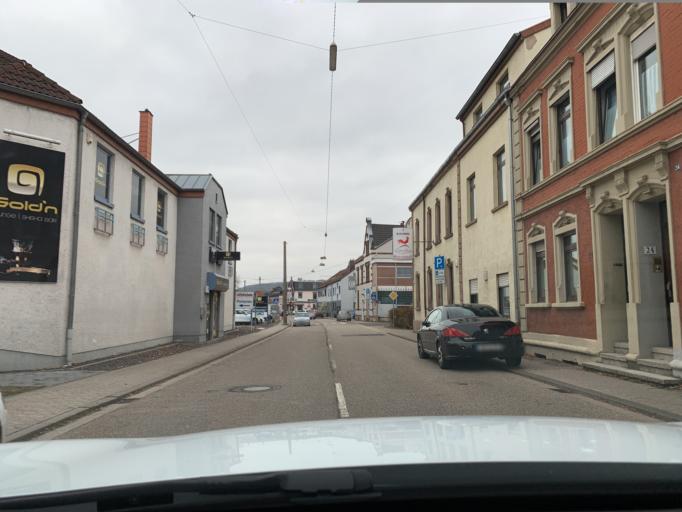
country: DE
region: Saarland
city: Kleinblittersdorf
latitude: 49.1590
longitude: 7.0346
